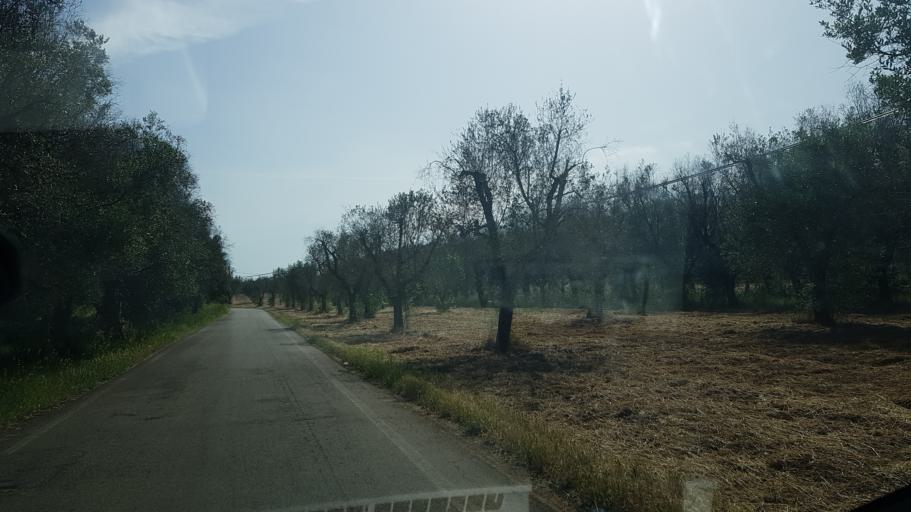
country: IT
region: Apulia
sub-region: Provincia di Brindisi
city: Torchiarolo
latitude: 40.5026
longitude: 18.0601
